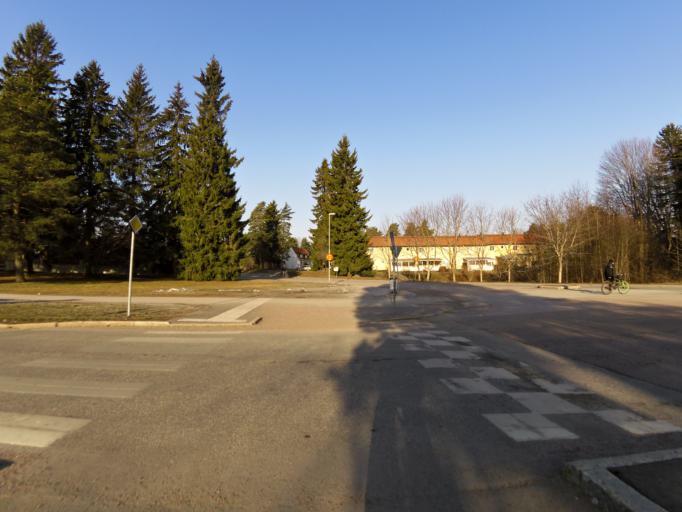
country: SE
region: Gaevleborg
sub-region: Gavle Kommun
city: Gavle
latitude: 60.6592
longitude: 17.1344
